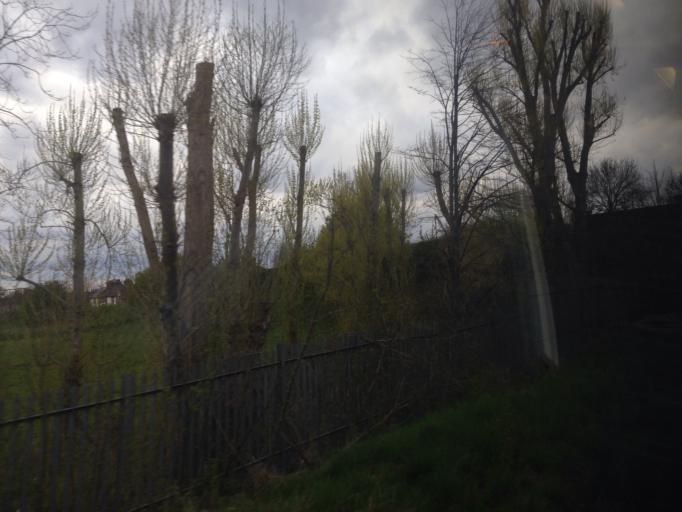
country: GB
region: England
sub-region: Greater London
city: Mitcham
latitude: 51.4025
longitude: -0.1578
